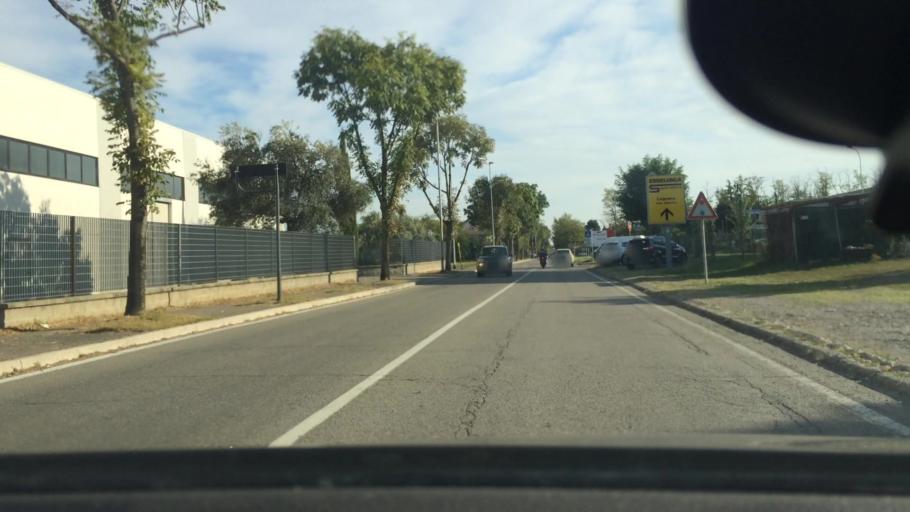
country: IT
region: Lombardy
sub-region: Provincia di Varese
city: Castellanza
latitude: 45.5976
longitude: 8.8959
